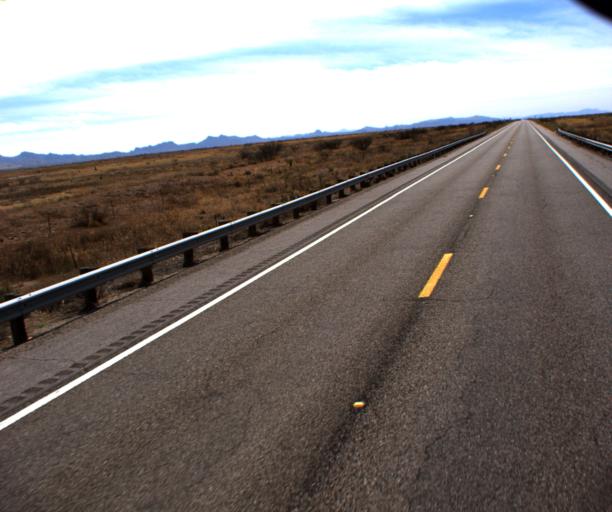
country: US
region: Arizona
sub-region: Cochise County
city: Pirtleville
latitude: 31.5288
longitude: -109.6505
